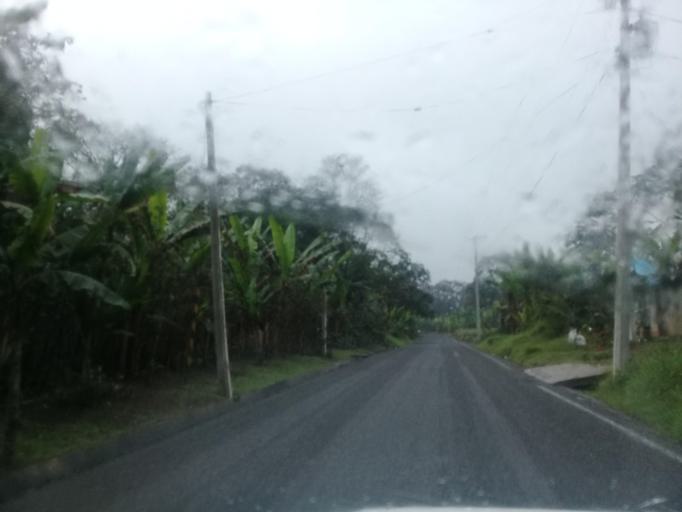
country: MX
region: Veracruz
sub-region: Amatlan de los Reyes
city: Centro de Readaptacion Social
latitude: 18.7992
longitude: -96.9392
